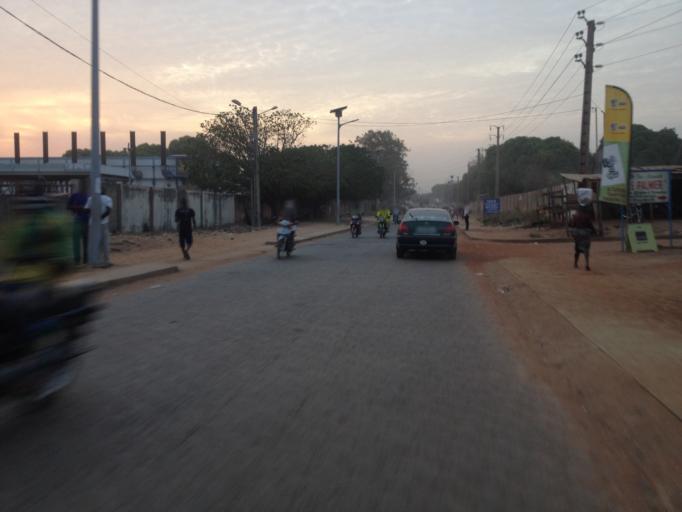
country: BJ
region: Borgou
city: Parakou
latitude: 9.3361
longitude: 2.6417
